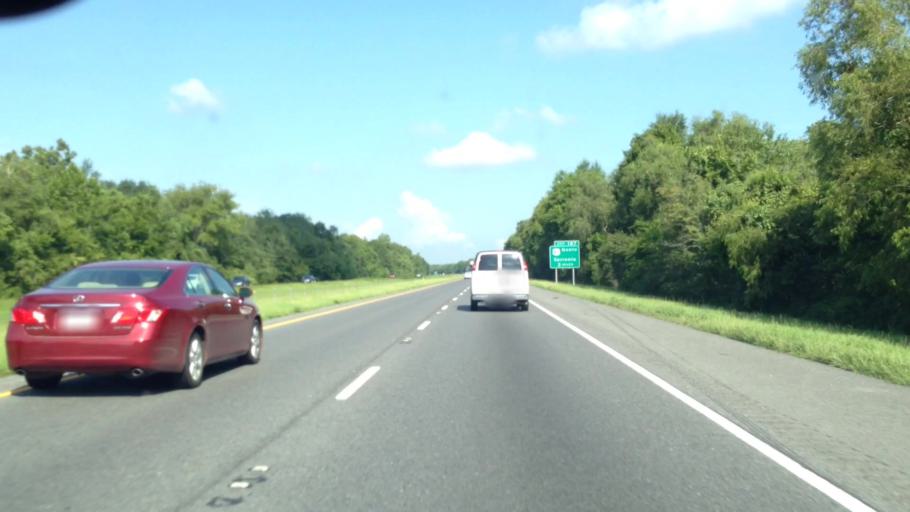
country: US
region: Louisiana
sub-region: Saint James Parish
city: Grand Point
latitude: 30.1459
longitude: -90.7665
